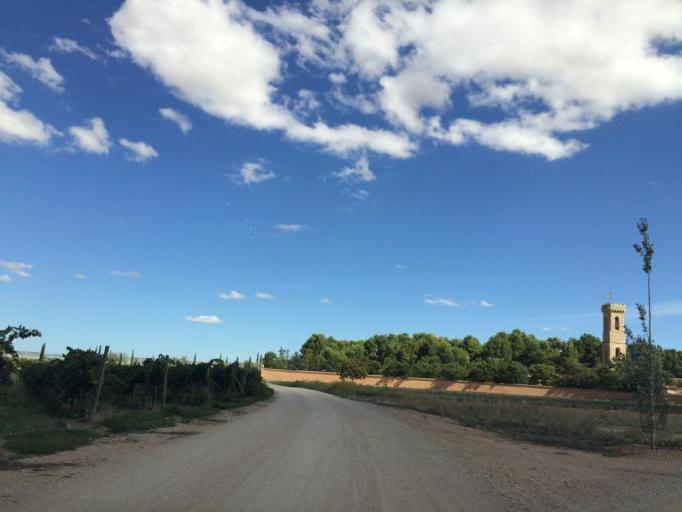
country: ES
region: Castille-La Mancha
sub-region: Provincia de Albacete
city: Albacete
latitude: 38.9294
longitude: -1.8642
